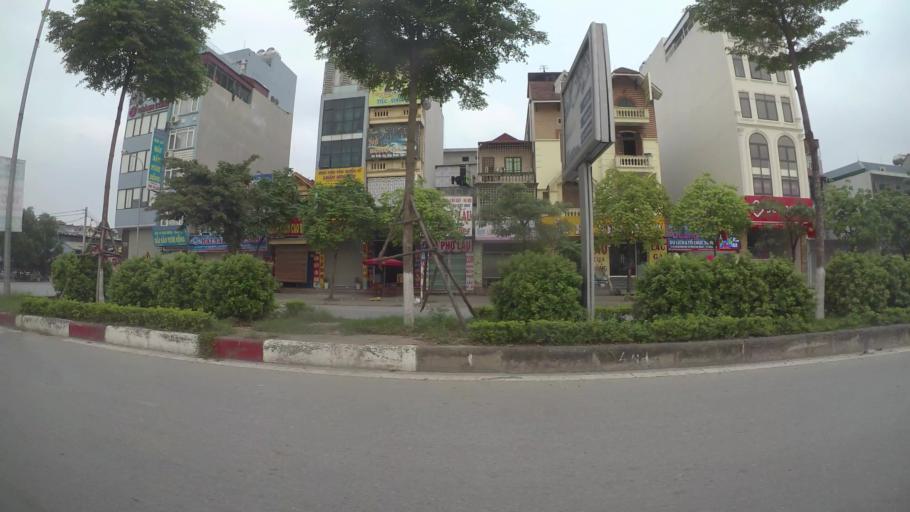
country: VN
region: Ha Noi
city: Cau Dien
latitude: 21.0421
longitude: 105.7734
